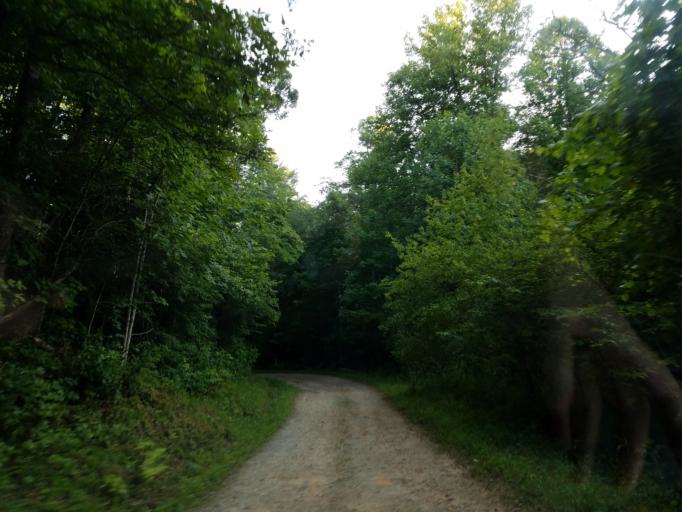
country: US
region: Georgia
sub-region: Lumpkin County
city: Dahlonega
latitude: 34.5854
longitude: -83.9756
